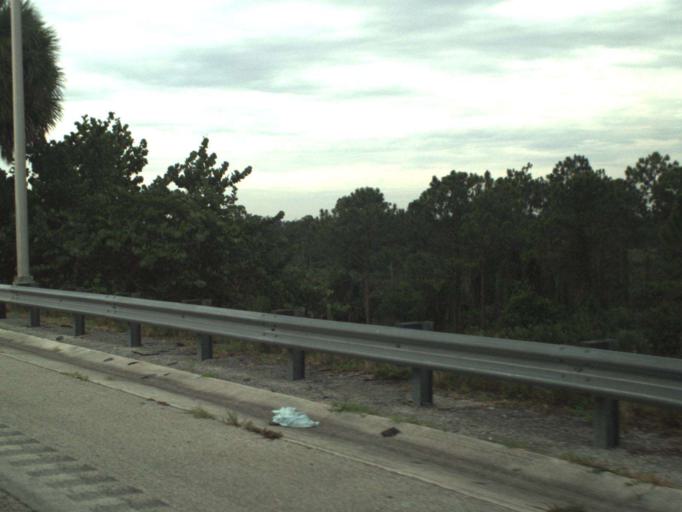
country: US
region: Florida
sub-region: Martin County
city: Palm City
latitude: 27.1256
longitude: -80.2827
